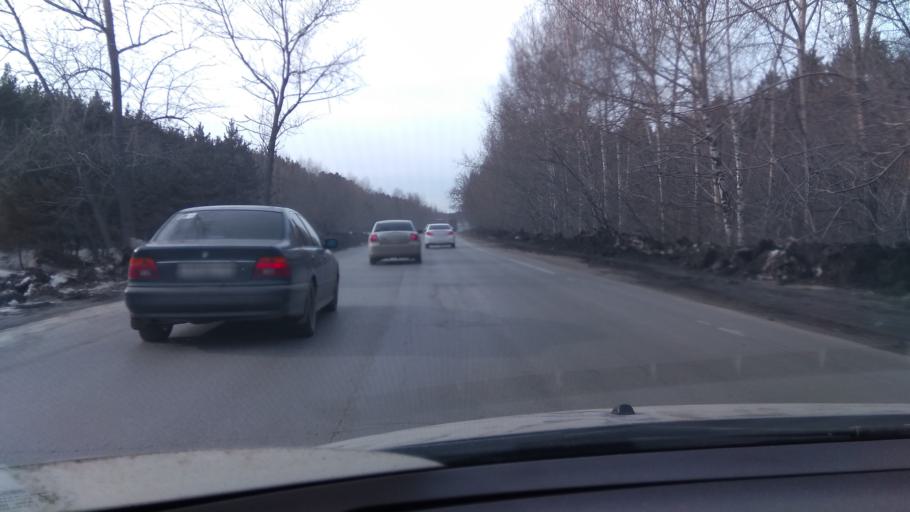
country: RU
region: Sverdlovsk
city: Sovkhoznyy
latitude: 56.8072
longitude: 60.5319
